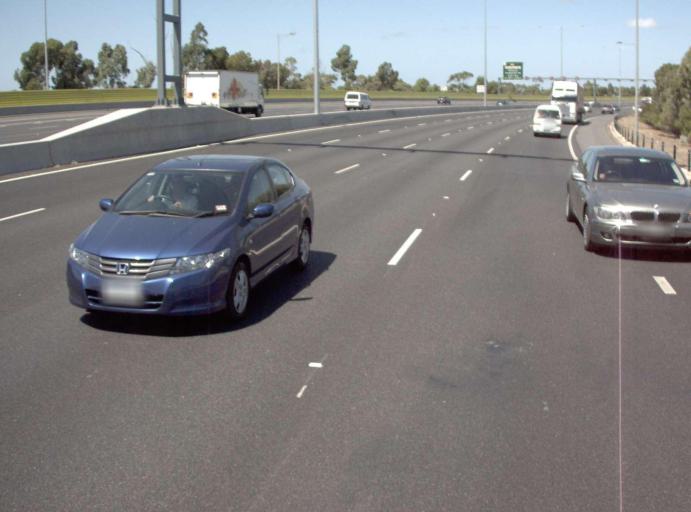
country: AU
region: Victoria
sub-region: Brimbank
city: Deer Park
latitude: -37.7758
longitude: 144.7939
